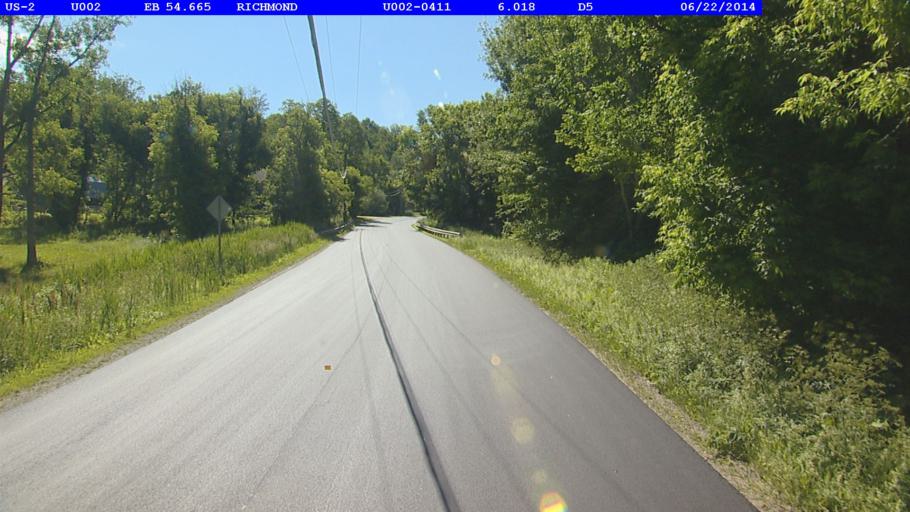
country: US
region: Vermont
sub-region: Chittenden County
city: Jericho
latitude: 44.3851
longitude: -72.9397
